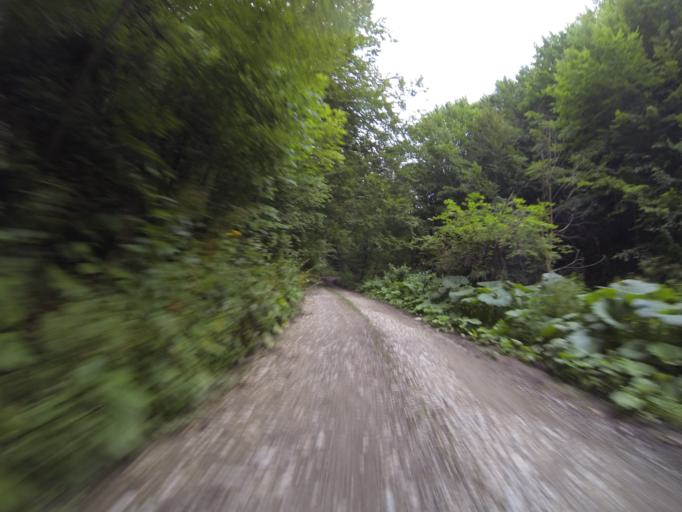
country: RO
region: Brasov
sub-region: Comuna Sinca Veche
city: Sinca Veche
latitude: 45.6853
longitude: 25.1399
